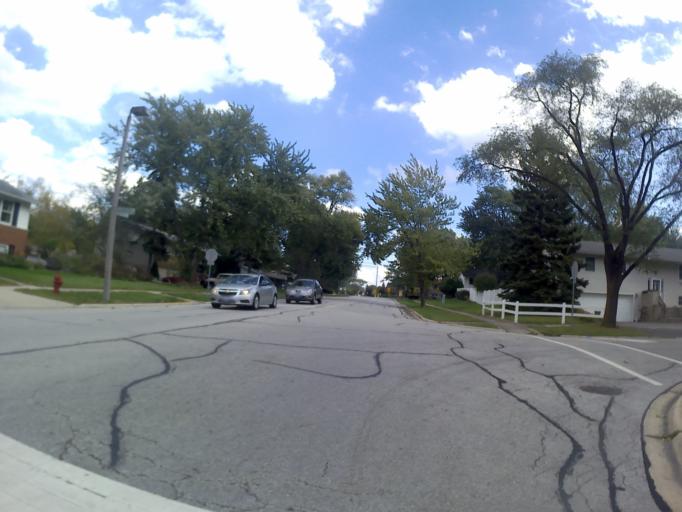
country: US
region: Illinois
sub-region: DuPage County
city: Woodridge
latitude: 41.7660
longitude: -88.0618
